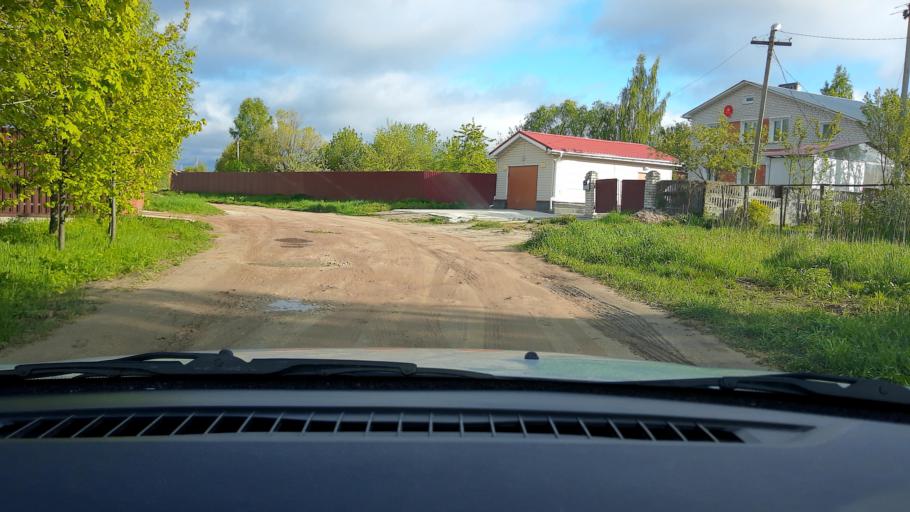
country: RU
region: Nizjnij Novgorod
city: Afonino
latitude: 56.1929
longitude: 44.0712
